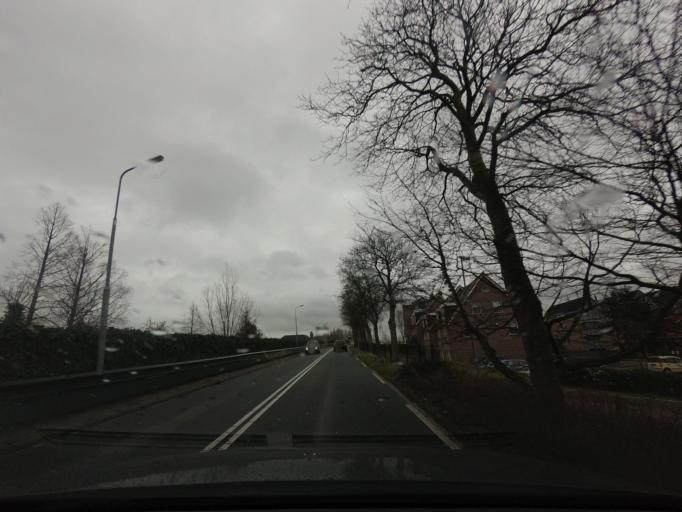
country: NL
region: North Holland
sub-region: Gemeente Langedijk
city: Broek op Langedijk
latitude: 52.6739
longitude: 4.8072
